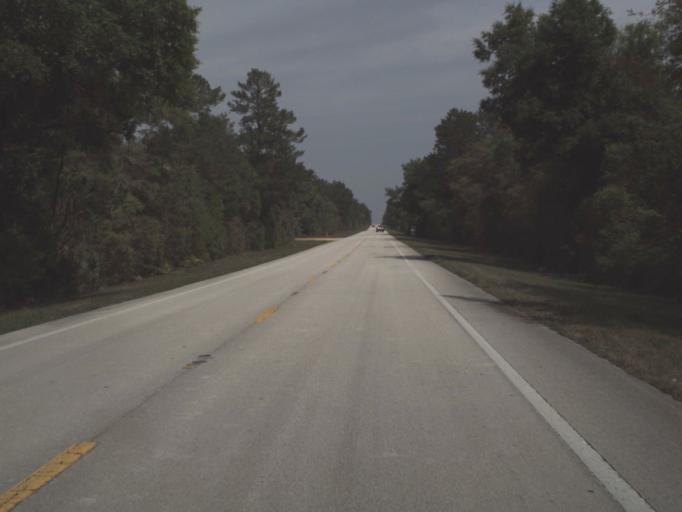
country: US
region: Florida
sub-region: Lake County
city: Astor
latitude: 29.2540
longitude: -81.6464
